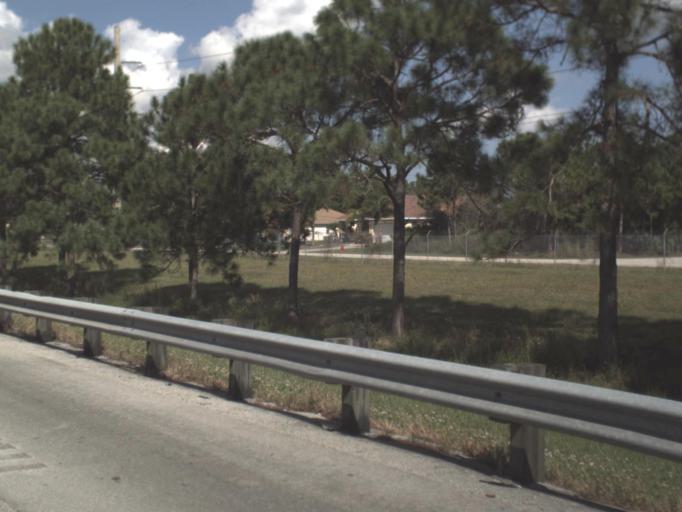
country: US
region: Florida
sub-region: Saint Lucie County
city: Port Saint Lucie
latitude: 27.2652
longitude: -80.3537
